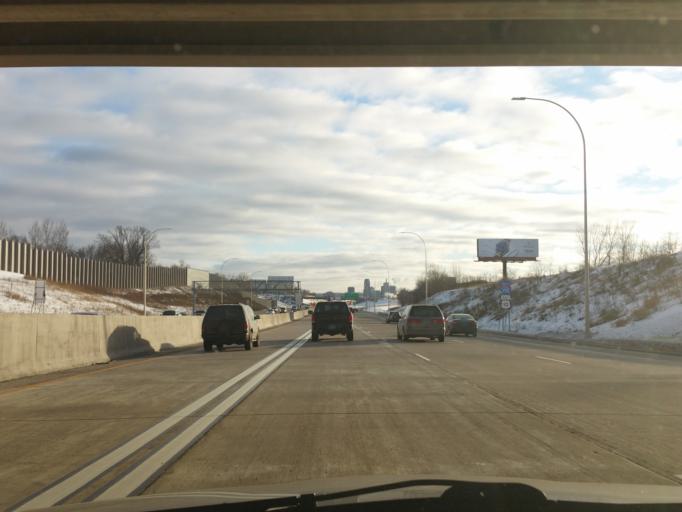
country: US
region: Minnesota
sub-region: Ramsey County
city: Saint Paul
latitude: 44.9847
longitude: -93.0891
